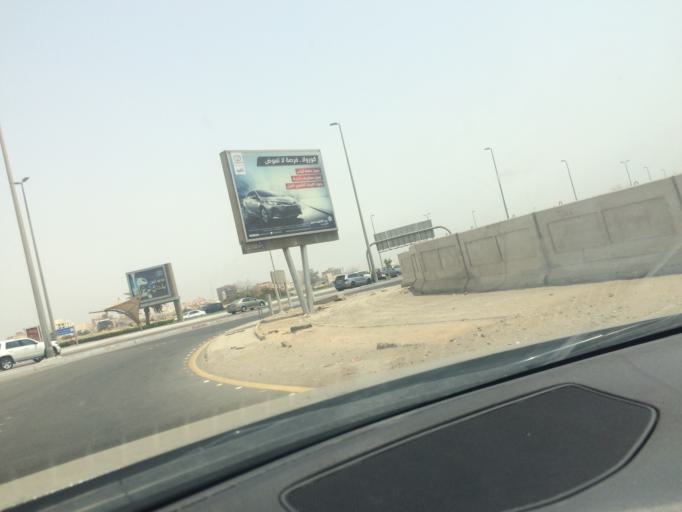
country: SA
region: Makkah
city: Jeddah
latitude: 21.5905
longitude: 39.1235
